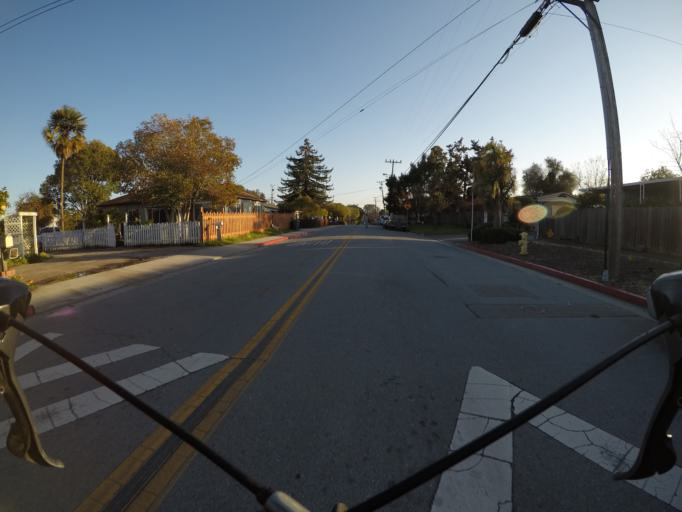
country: US
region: California
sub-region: Santa Cruz County
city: Live Oak
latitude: 36.9818
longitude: -121.9745
